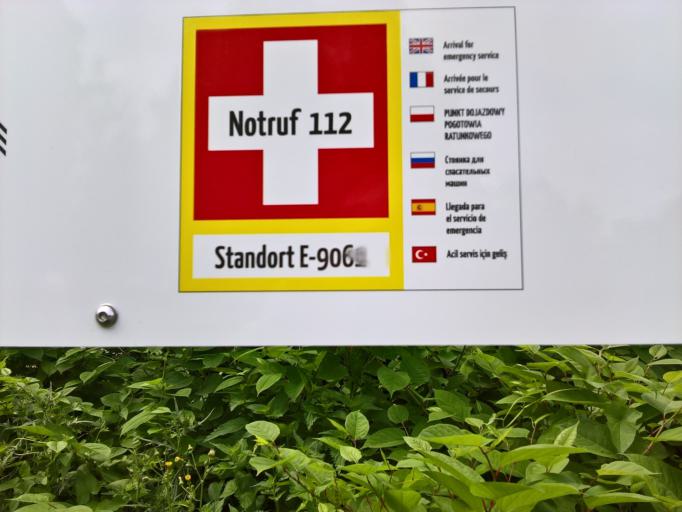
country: DE
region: North Rhine-Westphalia
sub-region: Regierungsbezirk Dusseldorf
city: Essen
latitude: 51.5165
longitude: 7.0245
